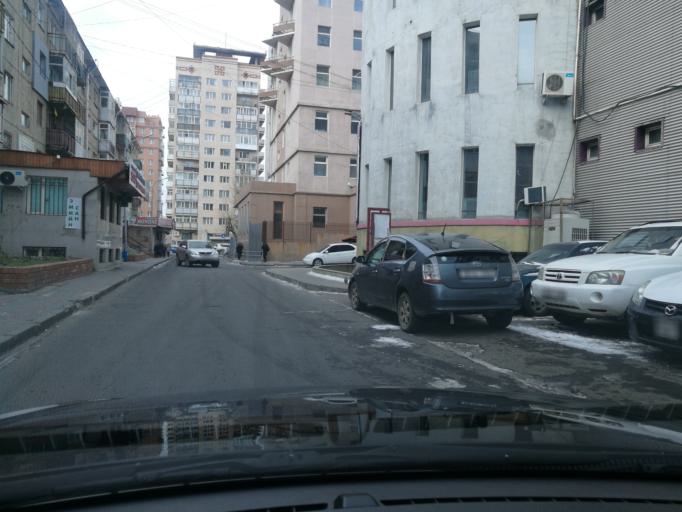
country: MN
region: Ulaanbaatar
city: Ulaanbaatar
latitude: 47.9126
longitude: 106.9031
